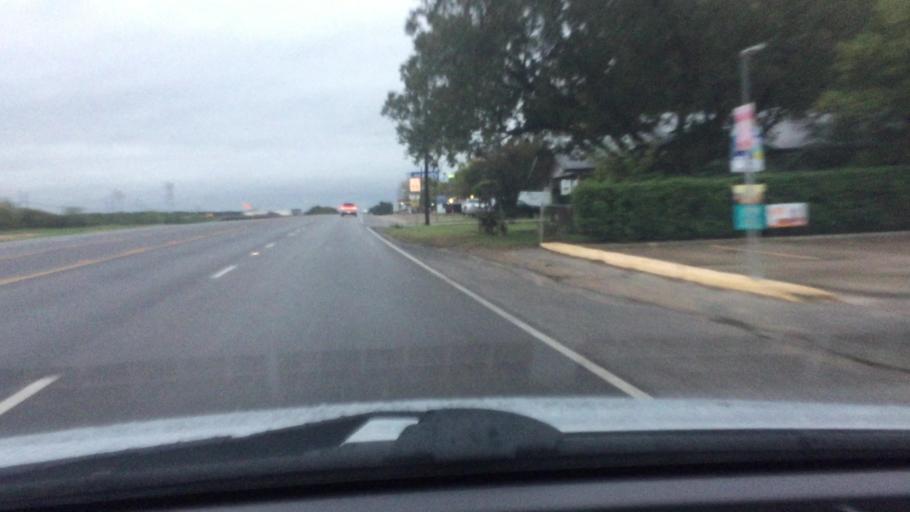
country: US
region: Texas
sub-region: Williamson County
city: Leander
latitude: 30.5782
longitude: -97.8527
